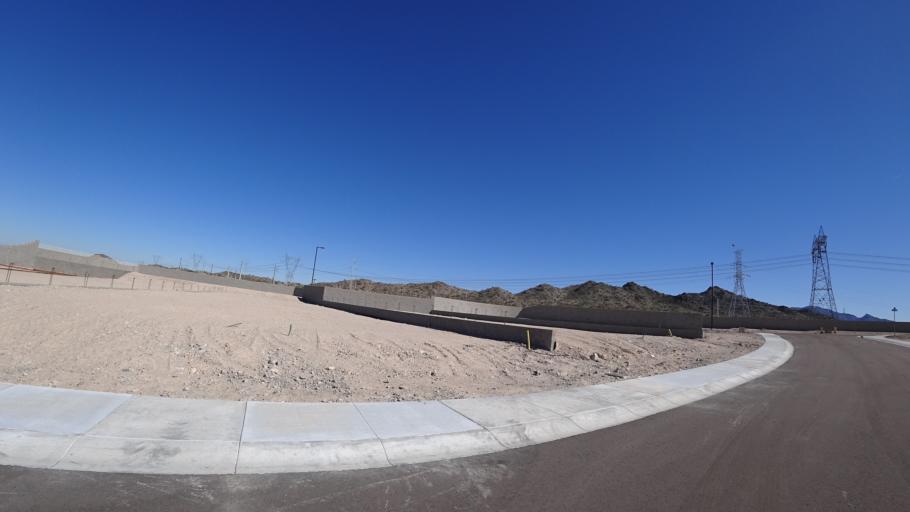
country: US
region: Arizona
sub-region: Maricopa County
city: Goodyear
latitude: 33.3485
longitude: -112.4247
